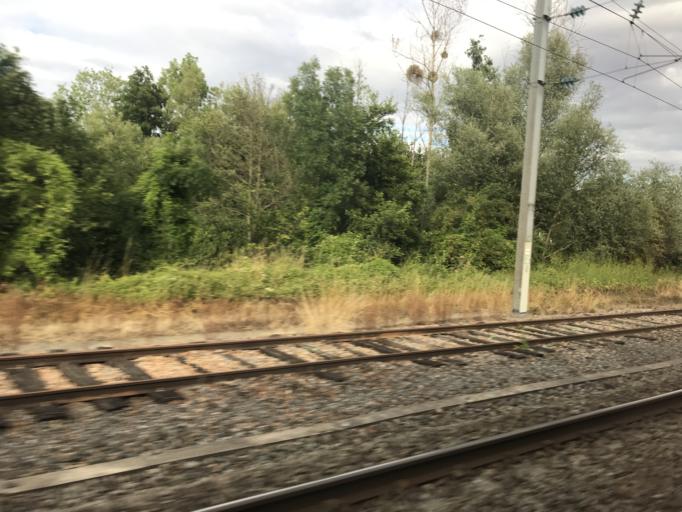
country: FR
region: Champagne-Ardenne
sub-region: Departement des Ardennes
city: Carignan
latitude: 49.6244
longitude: 5.1750
